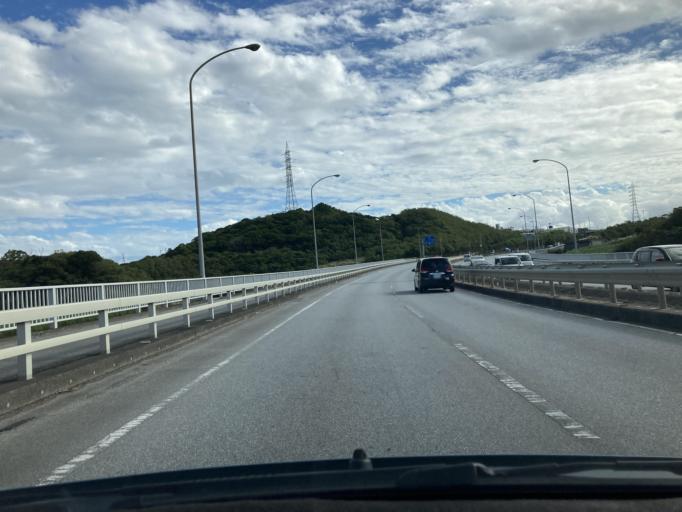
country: JP
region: Okinawa
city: Tomigusuku
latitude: 26.1775
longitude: 127.7268
